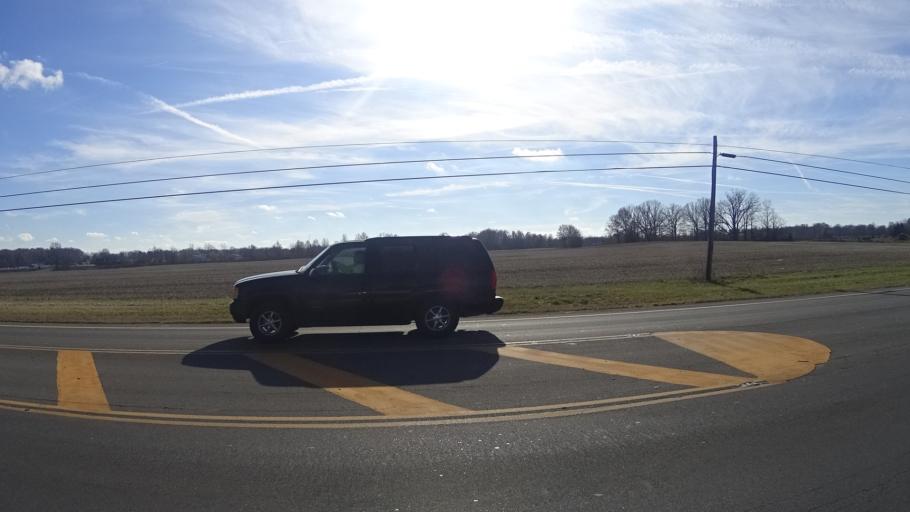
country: US
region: Ohio
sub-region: Lorain County
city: Eaton Estates
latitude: 41.3139
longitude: -81.9943
